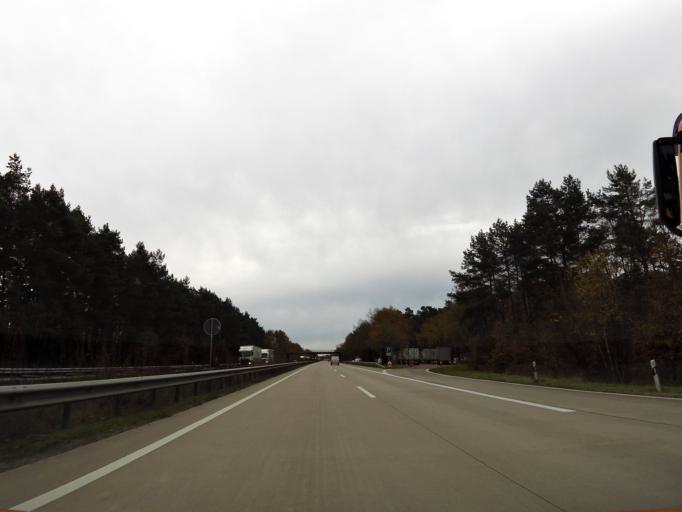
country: DE
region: Lower Saxony
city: Walsrode
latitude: 52.8257
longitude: 9.6082
